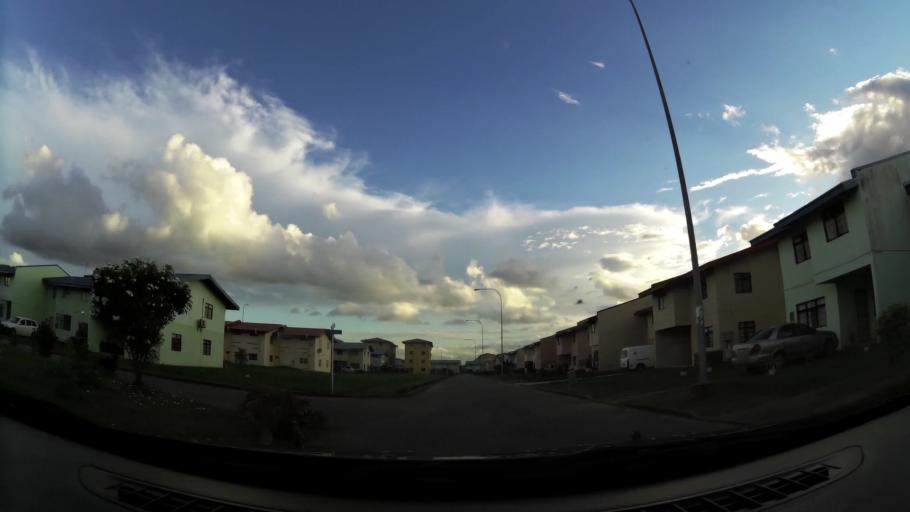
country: TT
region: Tunapuna/Piarco
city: Arouca
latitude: 10.6173
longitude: -61.3559
